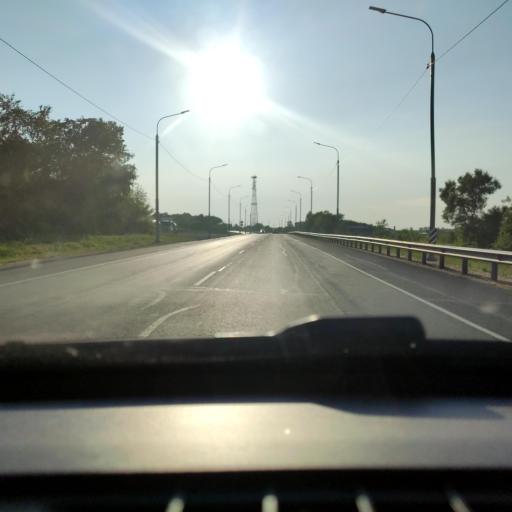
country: RU
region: Voronezj
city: Kashirskoye
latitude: 51.4990
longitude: 39.5833
